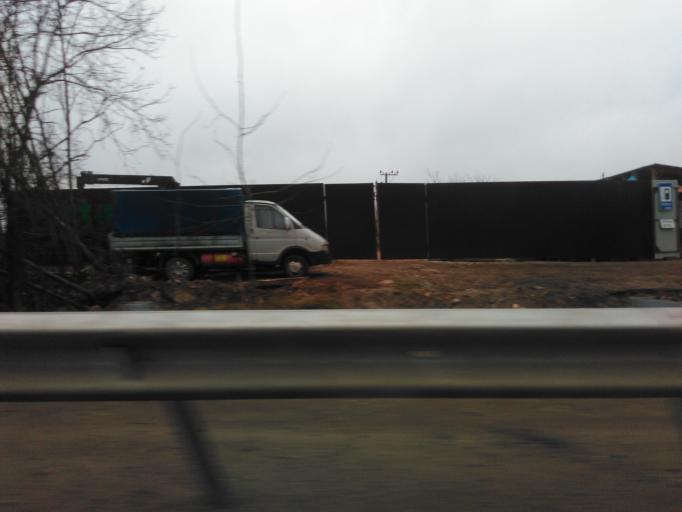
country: RU
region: Moskovskaya
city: Ashukino
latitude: 56.1377
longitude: 37.9858
